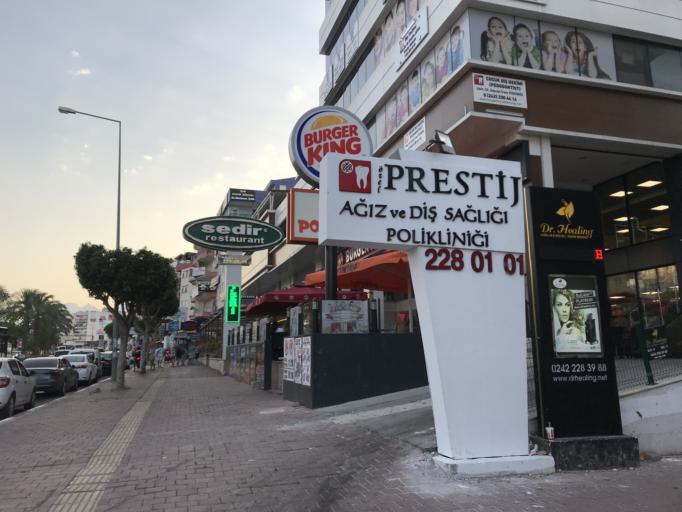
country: TR
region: Antalya
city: Antalya
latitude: 36.8765
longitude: 30.6445
